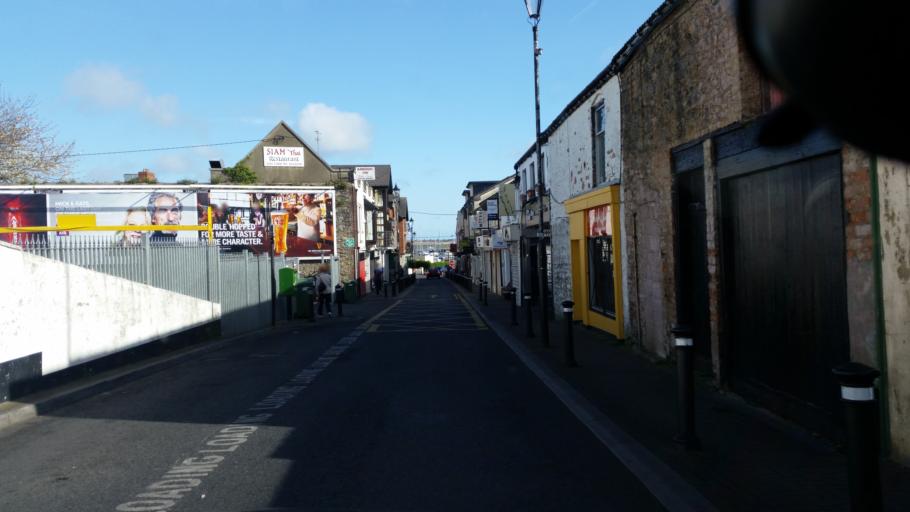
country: IE
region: Leinster
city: Malahide
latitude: 53.4512
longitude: -6.1525
